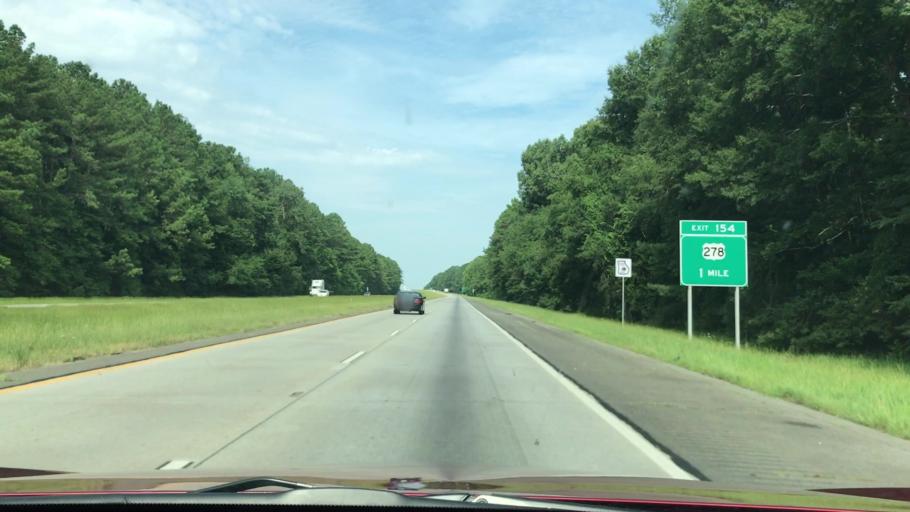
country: US
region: Georgia
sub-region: Warren County
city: Firing Range
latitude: 33.5005
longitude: -82.7886
